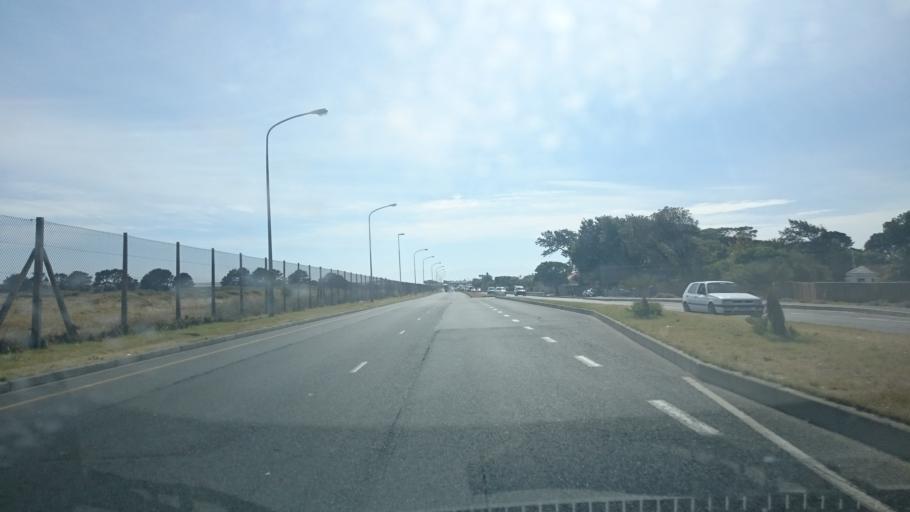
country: ZA
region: Western Cape
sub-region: City of Cape Town
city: Lansdowne
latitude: -34.0130
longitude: 18.4865
